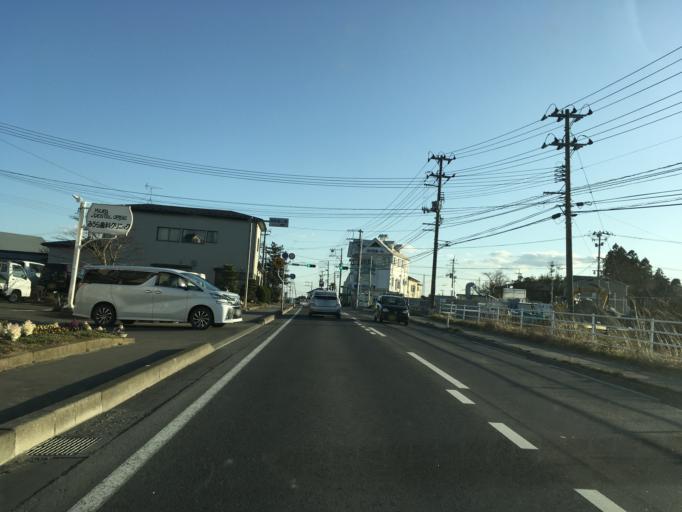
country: JP
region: Iwate
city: Ofunato
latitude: 38.8385
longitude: 141.5793
